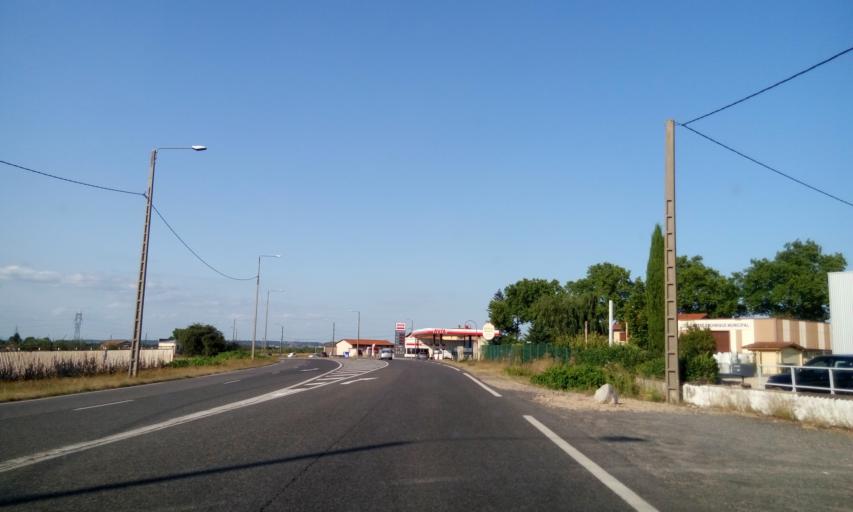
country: FR
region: Rhone-Alpes
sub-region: Departement du Rhone
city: Lissieu
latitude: 45.8728
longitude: 4.7467
